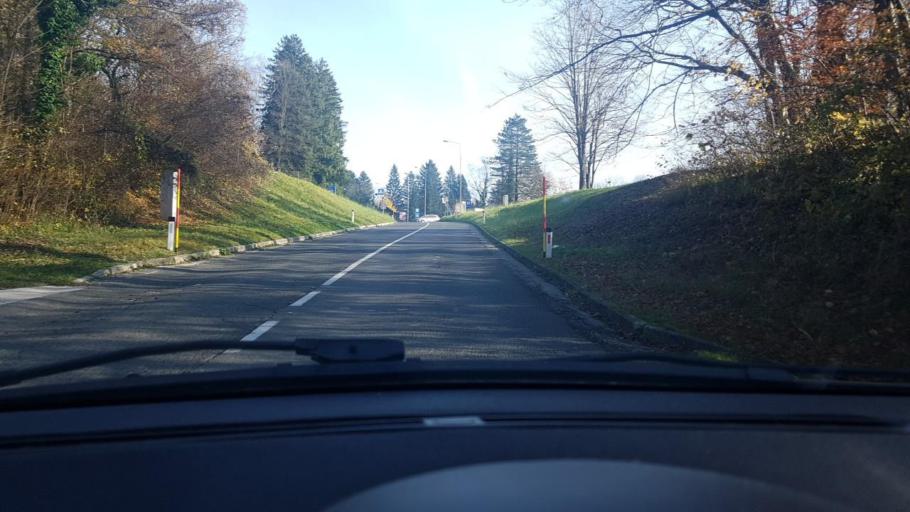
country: SI
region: Kranj
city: Golnik
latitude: 46.3277
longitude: 14.3290
